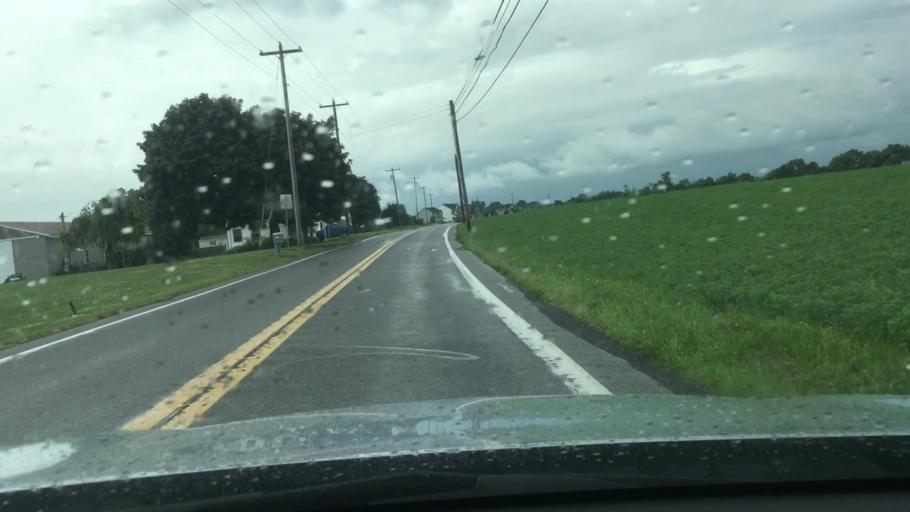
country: US
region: Pennsylvania
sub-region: Franklin County
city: Chambersburg
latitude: 39.8927
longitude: -77.7237
